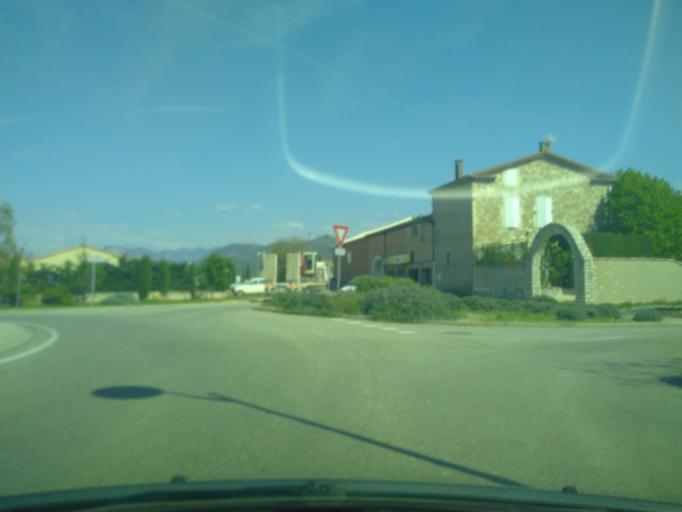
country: FR
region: Rhone-Alpes
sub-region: Departement de la Drome
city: La Begude-de-Mazenc
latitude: 44.6119
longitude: 4.9388
